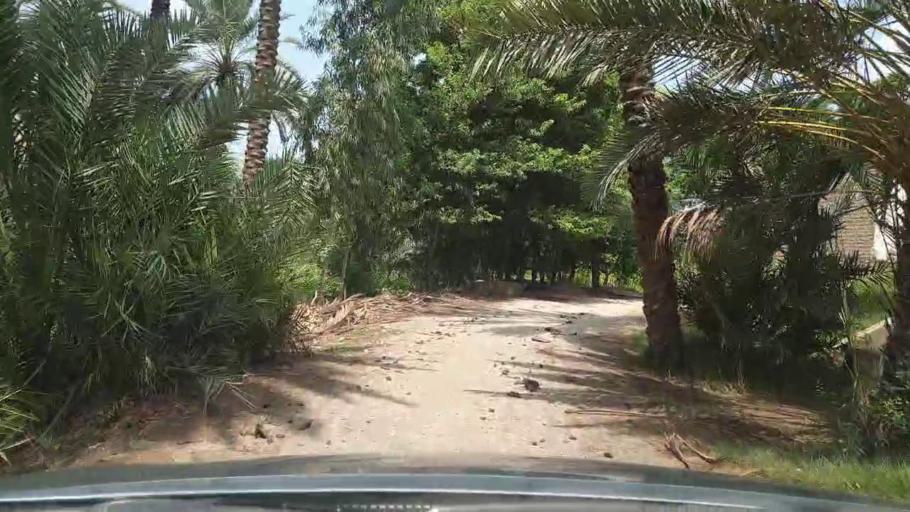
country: PK
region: Sindh
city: Pir jo Goth
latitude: 27.6168
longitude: 68.6635
